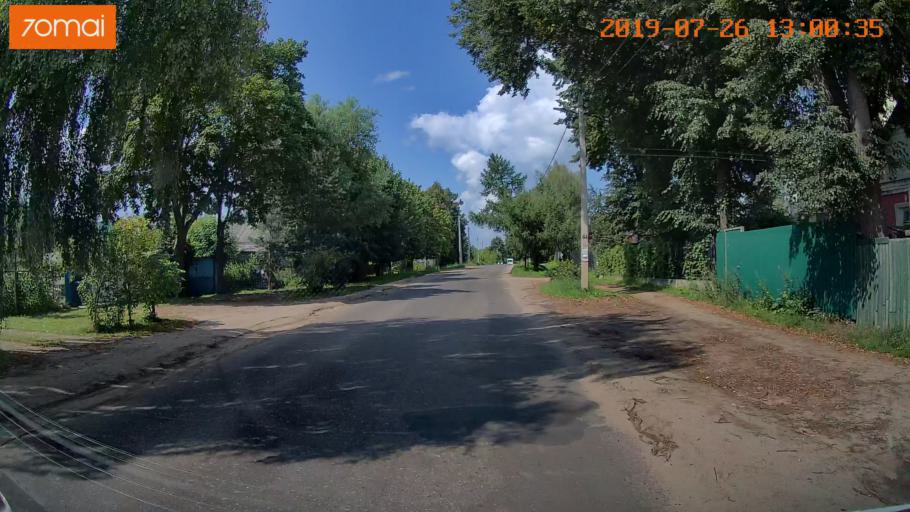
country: RU
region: Ivanovo
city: Bogorodskoye
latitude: 57.0342
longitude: 41.0152
